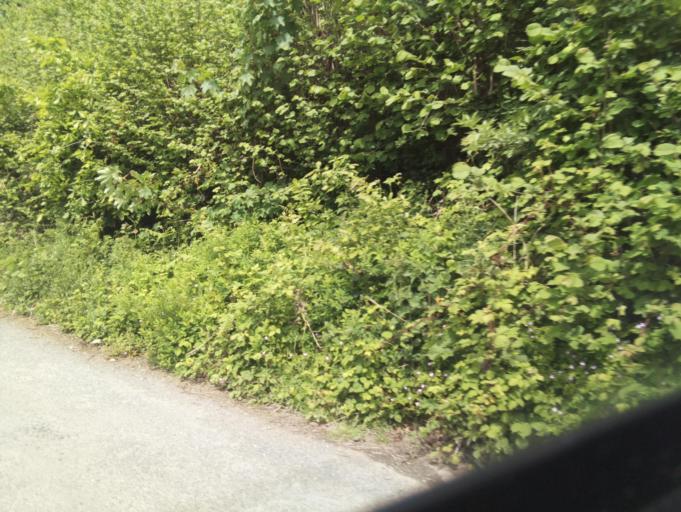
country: GB
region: England
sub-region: Devon
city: South Brent
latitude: 50.3659
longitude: -3.7858
